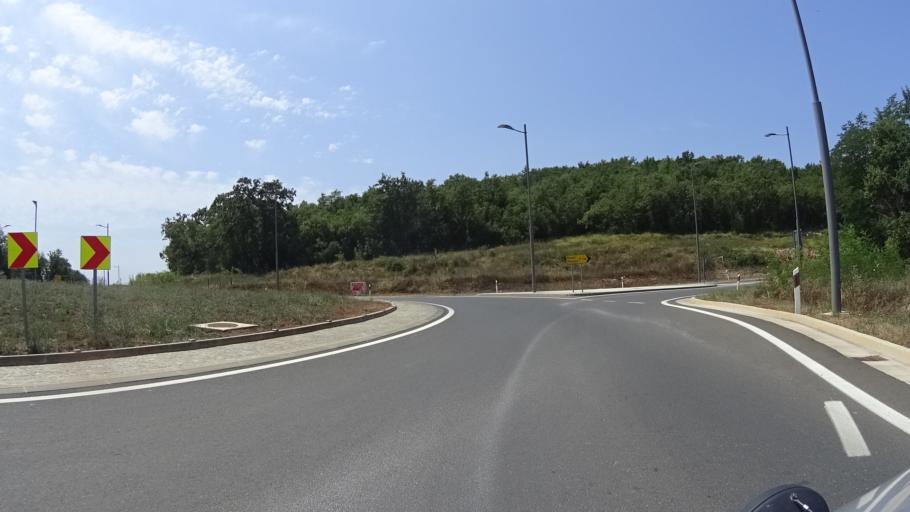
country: HR
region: Istarska
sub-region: Grad Porec
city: Porec
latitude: 45.2115
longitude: 13.6201
